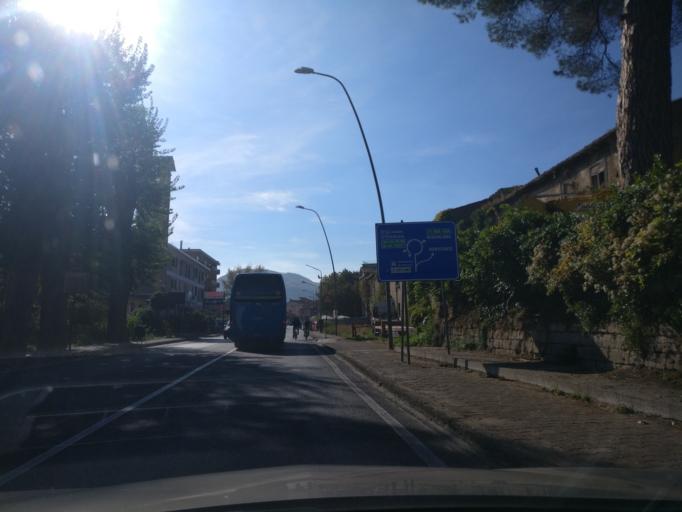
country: IT
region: Campania
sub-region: Provincia di Avellino
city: Torelli-Torrette
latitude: 40.9077
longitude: 14.7657
